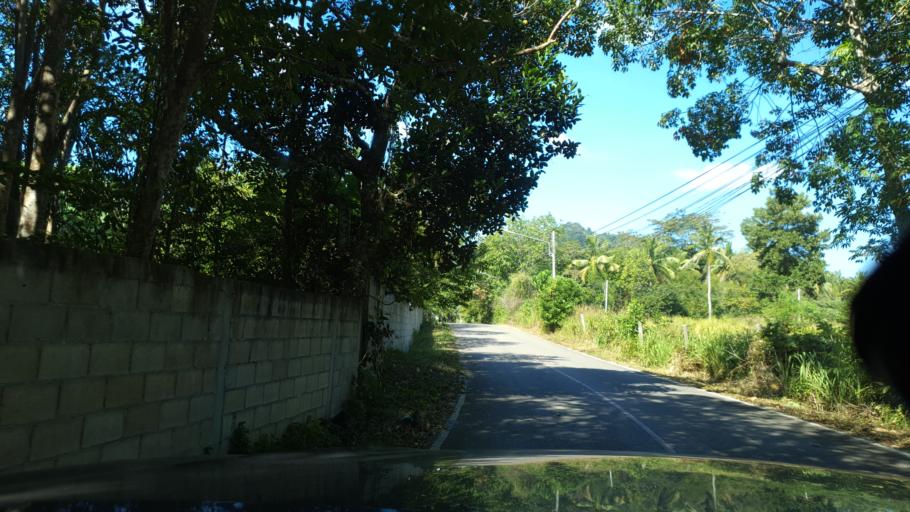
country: TH
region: Phangnga
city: Ban Ao Nang
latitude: 8.0299
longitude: 98.8596
